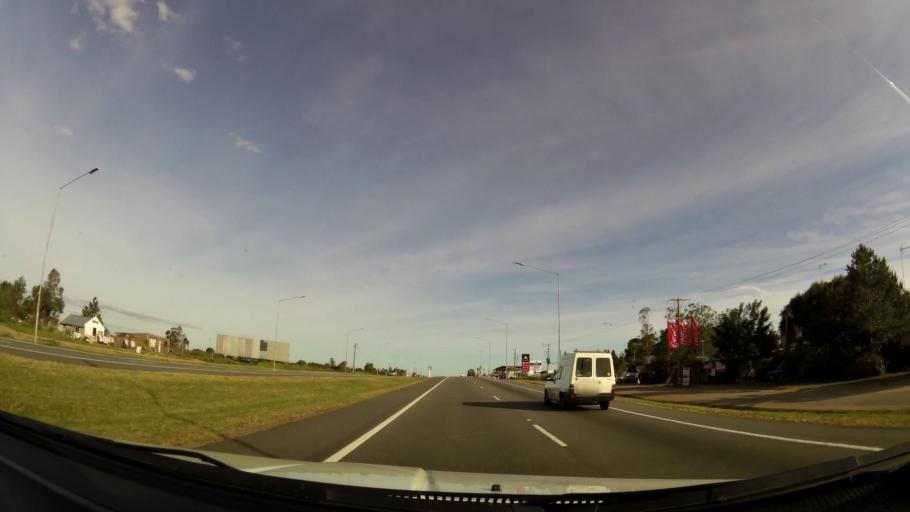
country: UY
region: Canelones
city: La Floresta
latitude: -34.7688
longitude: -55.5778
